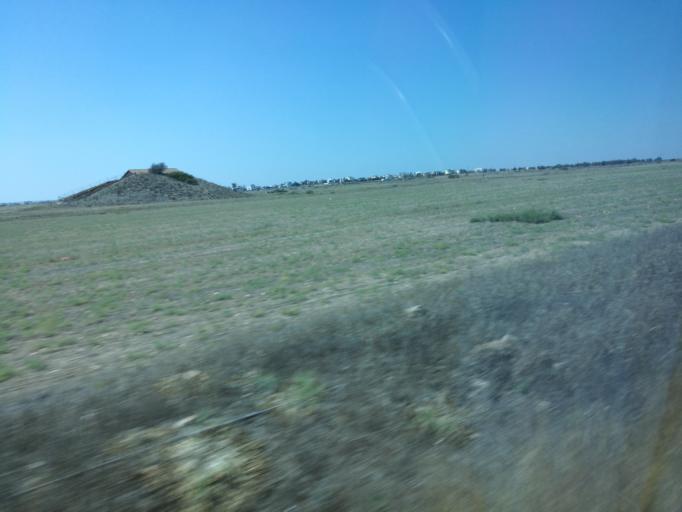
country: CY
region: Ammochostos
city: Famagusta
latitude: 35.1767
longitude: 33.8900
